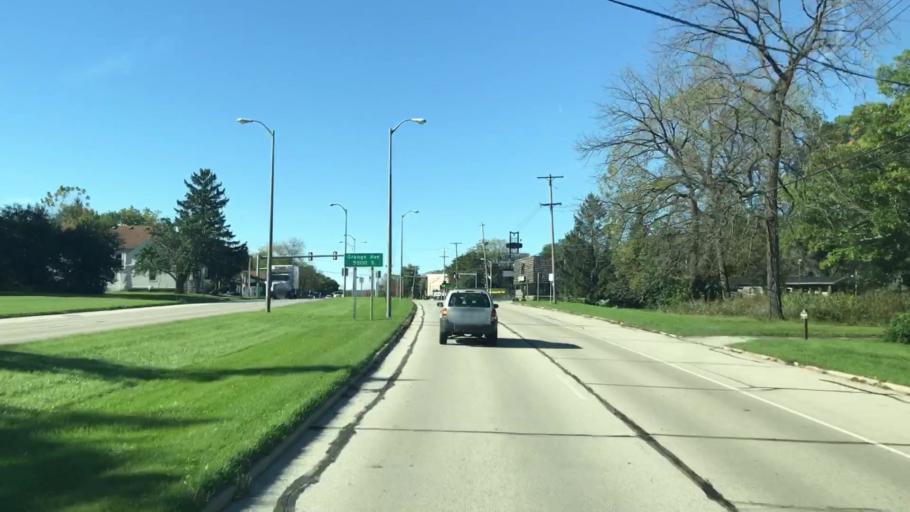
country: US
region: Wisconsin
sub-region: Milwaukee County
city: Hales Corners
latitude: 42.9458
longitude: -88.0348
